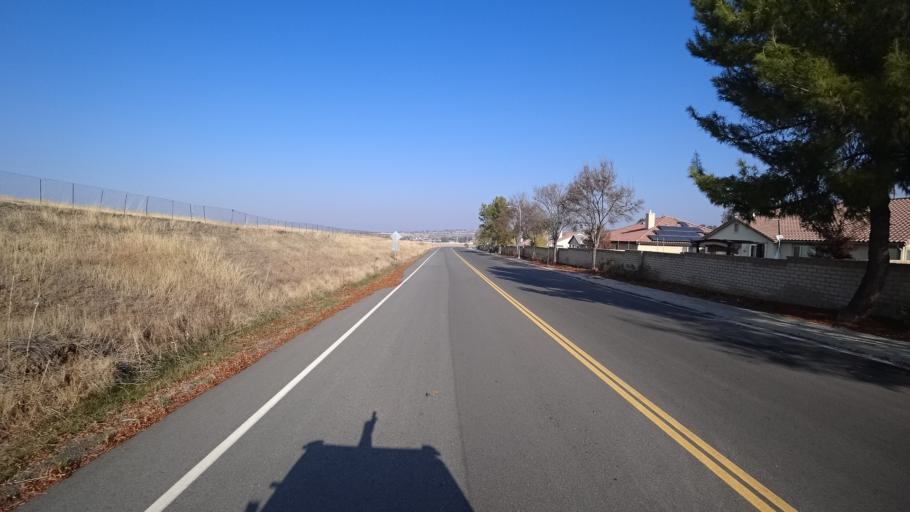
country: US
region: California
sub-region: Kern County
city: Lamont
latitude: 35.3993
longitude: -118.8450
